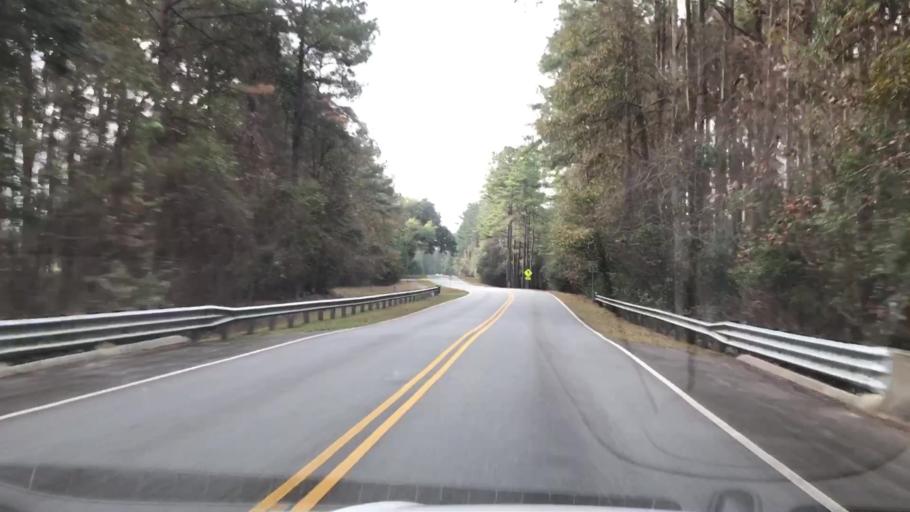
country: US
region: South Carolina
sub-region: Beaufort County
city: Bluffton
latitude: 32.2806
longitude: -80.9276
